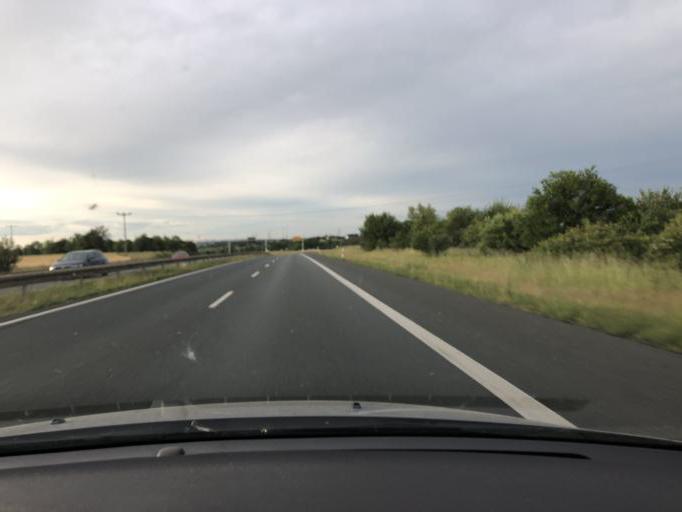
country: DE
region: Saxony-Anhalt
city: Burgwerben
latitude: 51.2094
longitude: 11.9982
